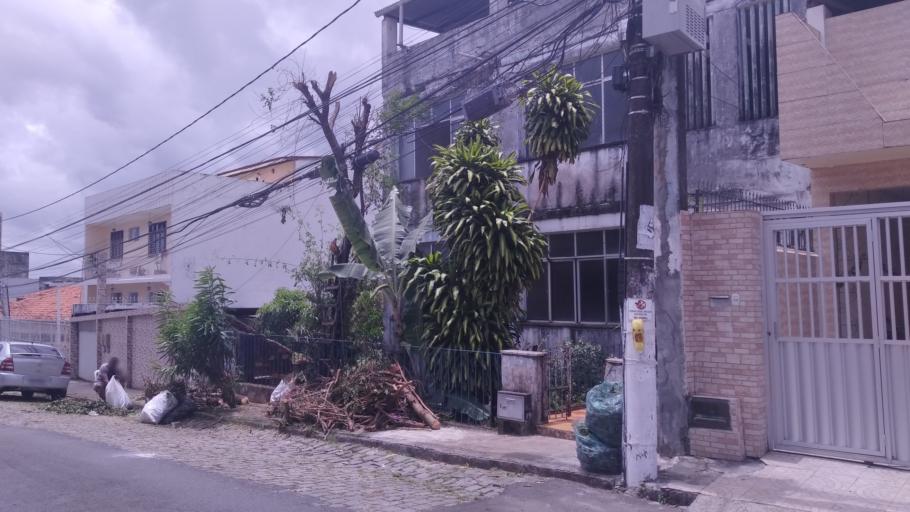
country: BR
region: Bahia
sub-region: Salvador
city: Salvador
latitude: -12.9715
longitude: -38.4971
